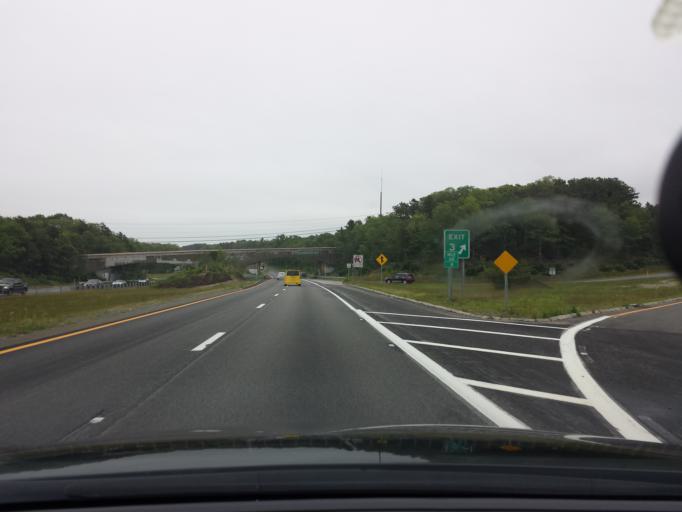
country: US
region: Massachusetts
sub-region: Barnstable County
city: East Sandwich
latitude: 41.7313
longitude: -70.4592
